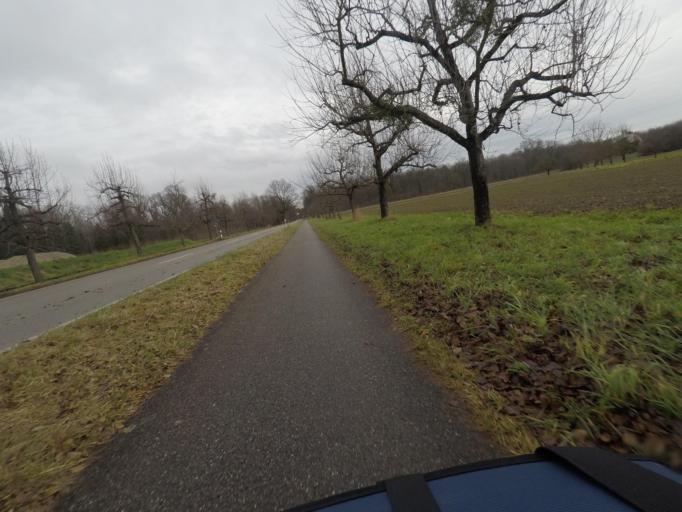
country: DE
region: Baden-Wuerttemberg
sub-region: Karlsruhe Region
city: Au am Rhein
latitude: 48.9618
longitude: 8.2484
